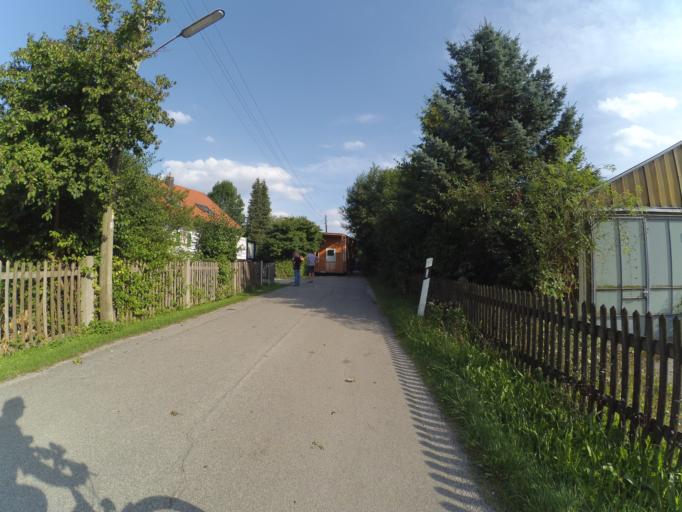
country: DE
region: Bavaria
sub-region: Upper Bavaria
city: Karlsfeld
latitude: 48.1886
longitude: 11.4961
